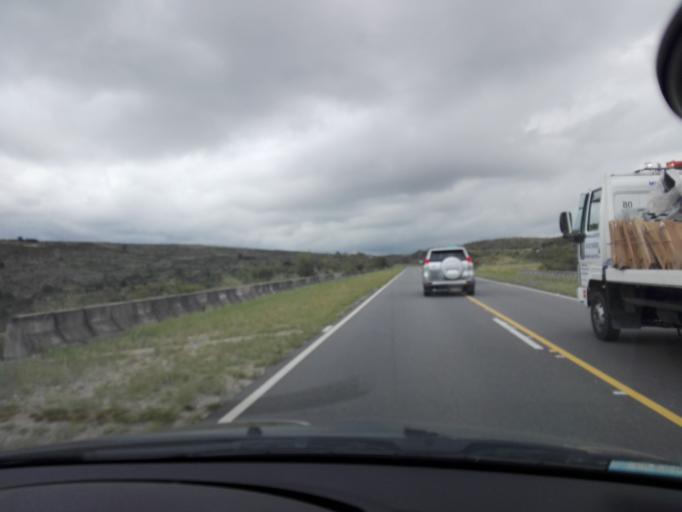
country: AR
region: Cordoba
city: Cuesta Blanca
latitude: -31.5731
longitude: -64.6456
